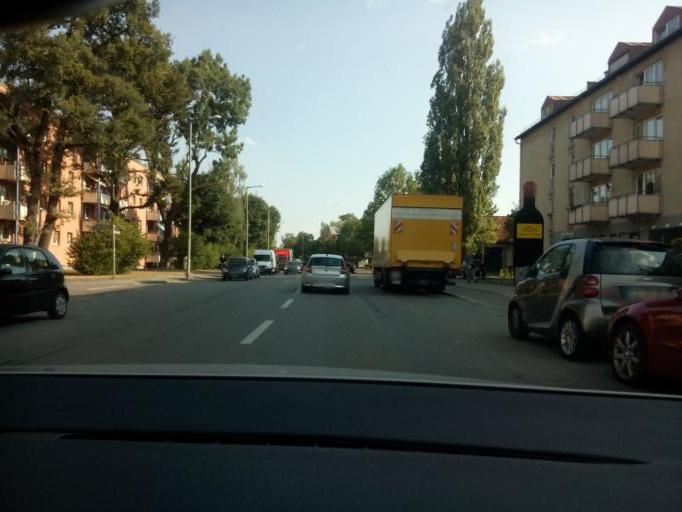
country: DE
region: Bavaria
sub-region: Upper Bavaria
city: Munich
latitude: 48.1068
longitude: 11.6043
